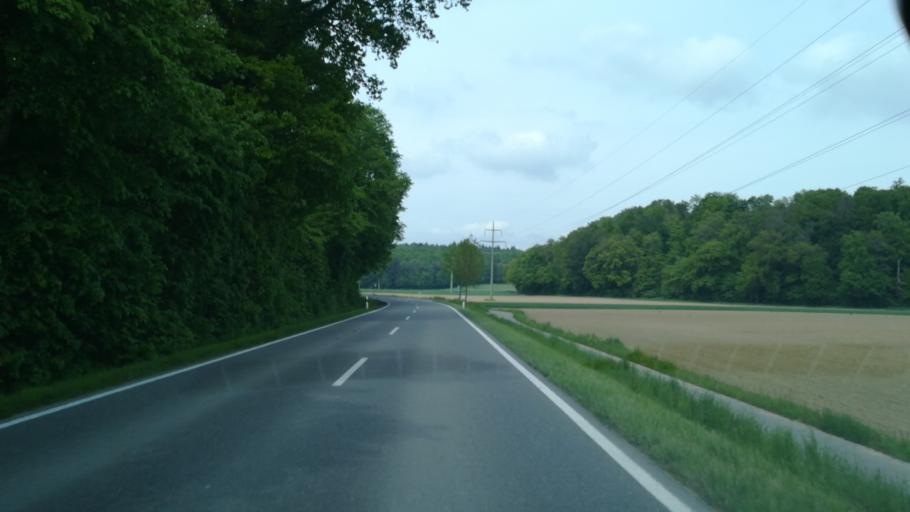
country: DE
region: Baden-Wuerttemberg
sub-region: Freiburg Region
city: Steisslingen
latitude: 47.7763
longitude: 8.8952
